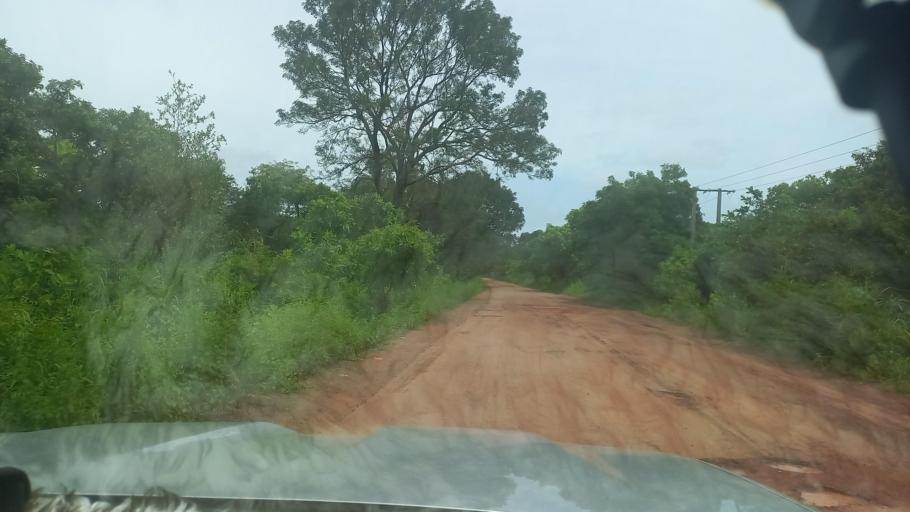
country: SN
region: Kolda
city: Marsassoum
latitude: 12.9051
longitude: -16.0180
